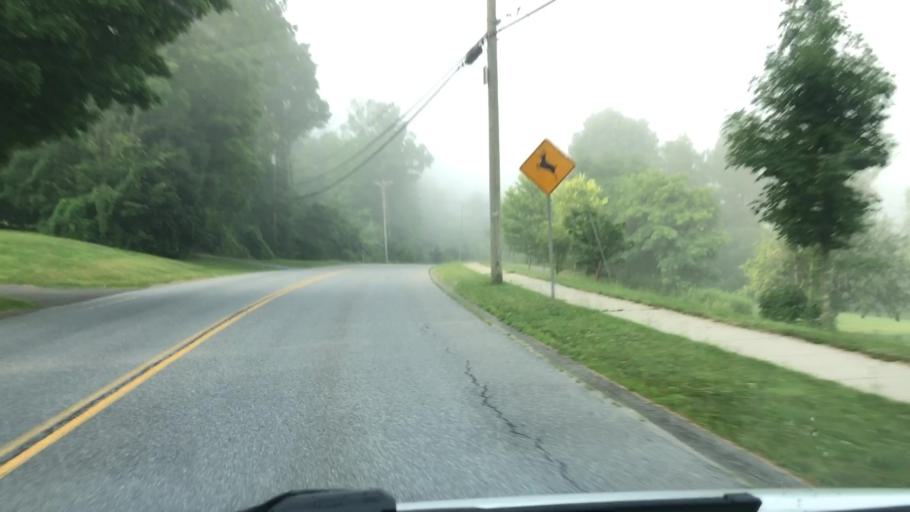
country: US
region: Massachusetts
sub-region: Berkshire County
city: Dalton
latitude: 42.4559
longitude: -73.1827
